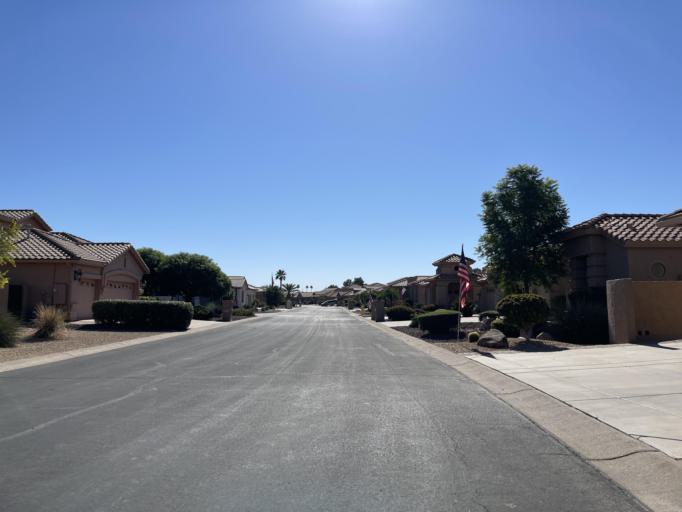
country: US
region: Arizona
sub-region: Maricopa County
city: Sun Lakes
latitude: 33.2265
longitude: -111.8880
